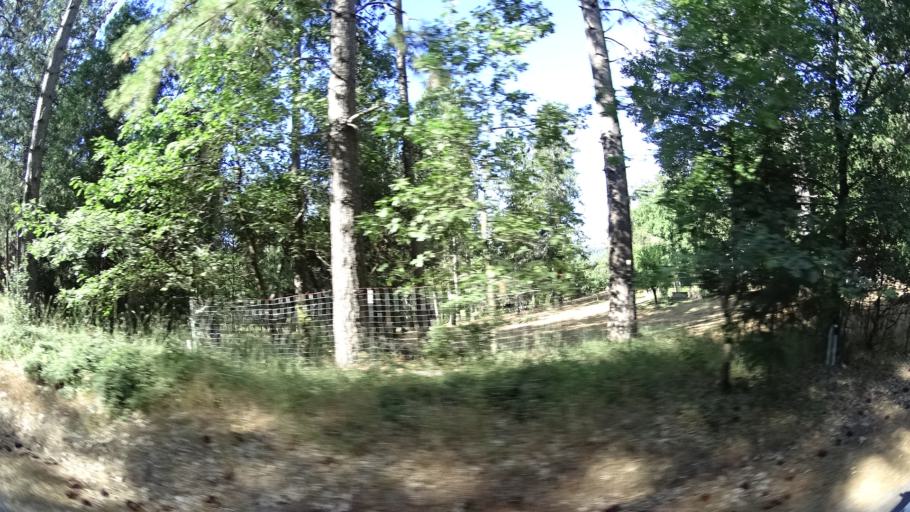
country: US
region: California
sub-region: Amador County
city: Pioneer
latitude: 38.3767
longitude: -120.4930
